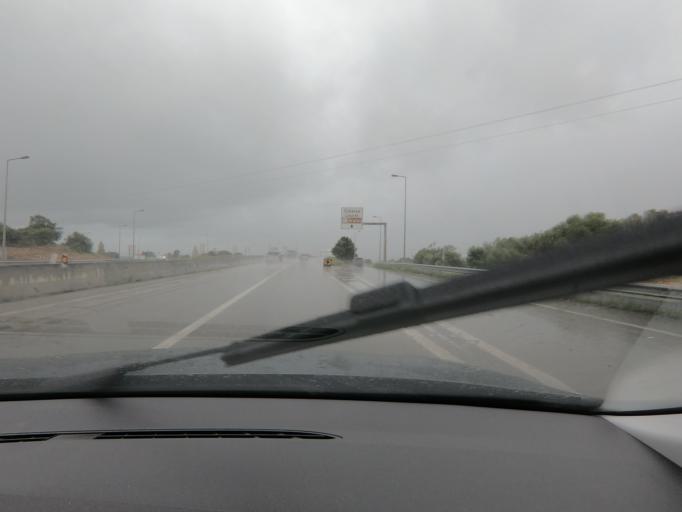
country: PT
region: Lisbon
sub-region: Sintra
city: Sintra
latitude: 38.8155
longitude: -9.3586
